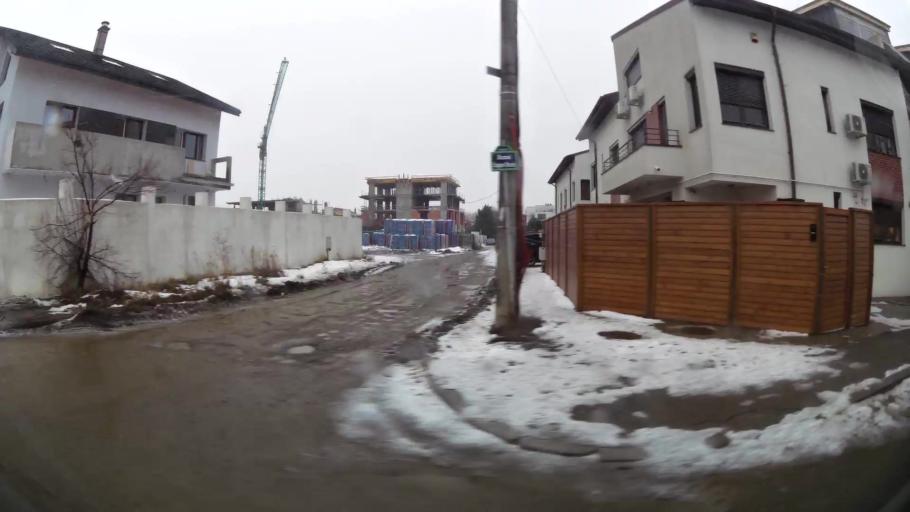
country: RO
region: Ilfov
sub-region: Comuna Otopeni
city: Otopeni
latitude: 44.5008
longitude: 26.0579
